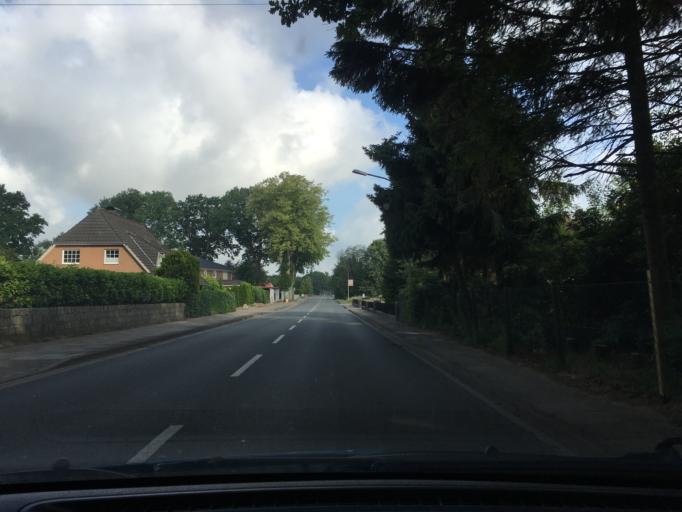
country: DE
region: Lower Saxony
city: Buchholz in der Nordheide
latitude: 53.3271
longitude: 9.8398
